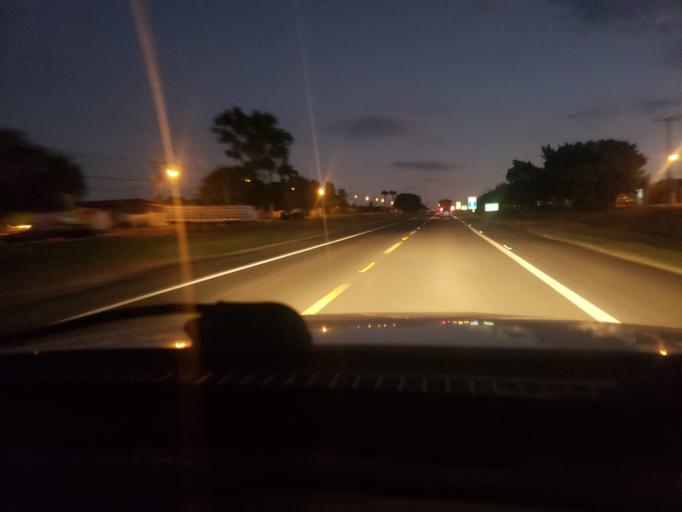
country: BR
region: Sao Paulo
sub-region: Conchal
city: Conchal
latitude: -22.3384
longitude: -47.1566
